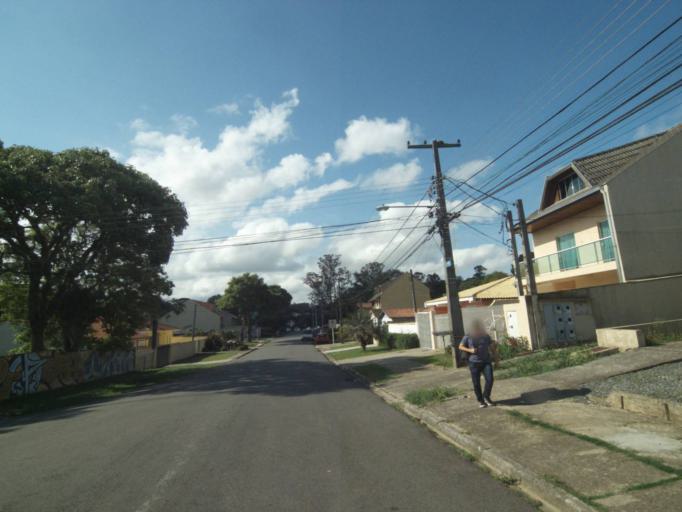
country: BR
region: Parana
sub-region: Curitiba
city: Curitiba
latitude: -25.3889
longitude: -49.3012
